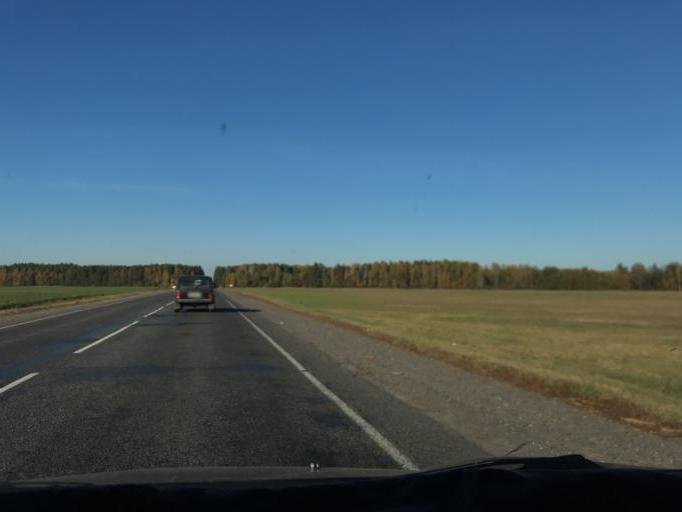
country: BY
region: Gomel
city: Kalinkavichy
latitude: 52.0494
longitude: 29.3611
